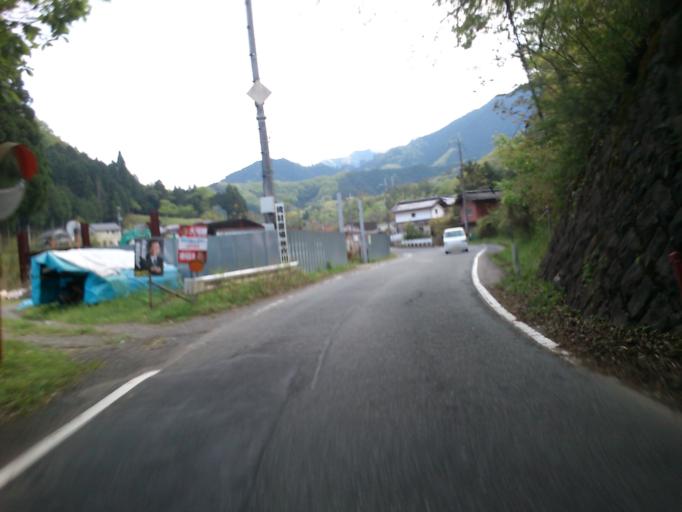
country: JP
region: Kyoto
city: Fukuchiyama
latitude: 35.3234
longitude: 134.9583
